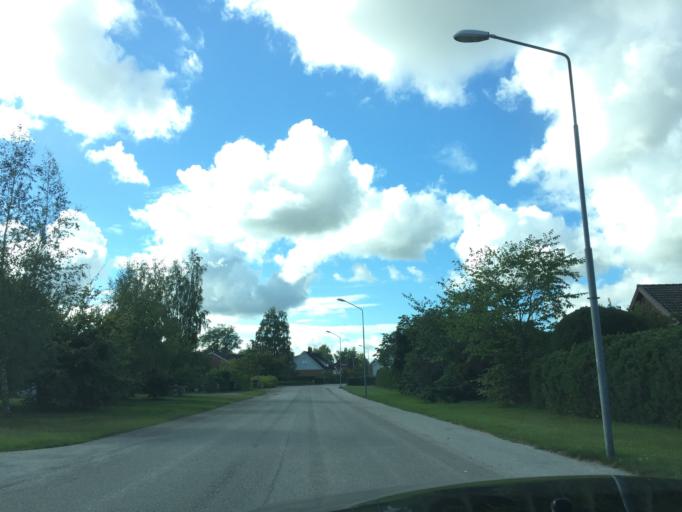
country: SE
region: Skane
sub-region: Sjobo Kommun
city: Sjoebo
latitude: 55.6330
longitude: 13.7145
